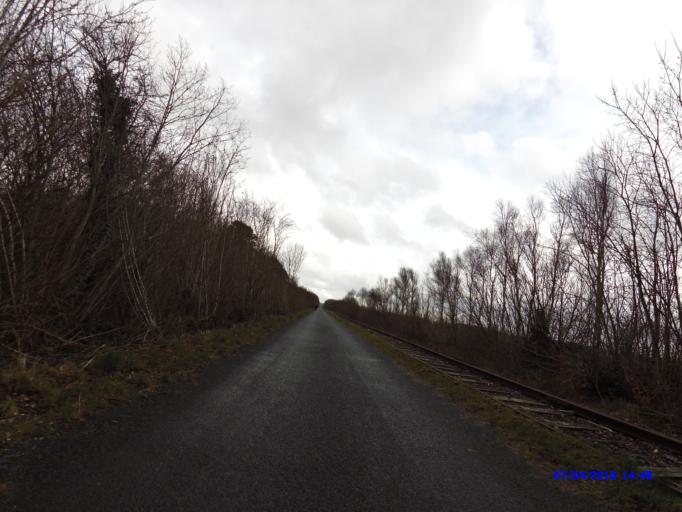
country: IE
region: Leinster
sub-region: An Iarmhi
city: Athlone
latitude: 53.4165
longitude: -7.8665
